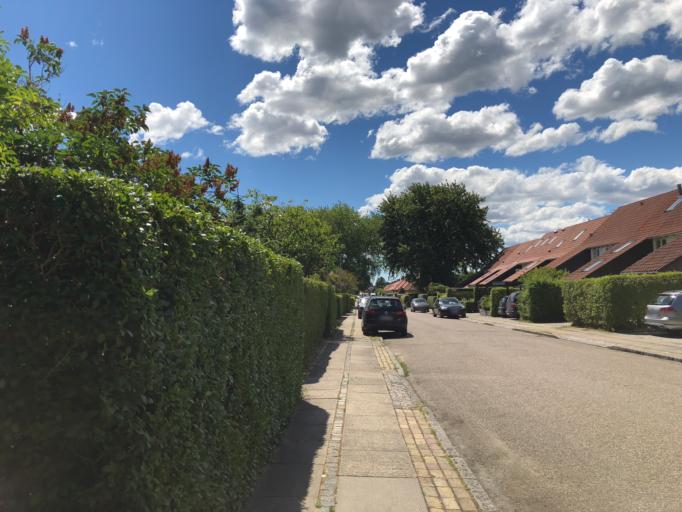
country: DK
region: Capital Region
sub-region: Rudersdal Kommune
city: Holte
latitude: 55.7861
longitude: 12.4685
